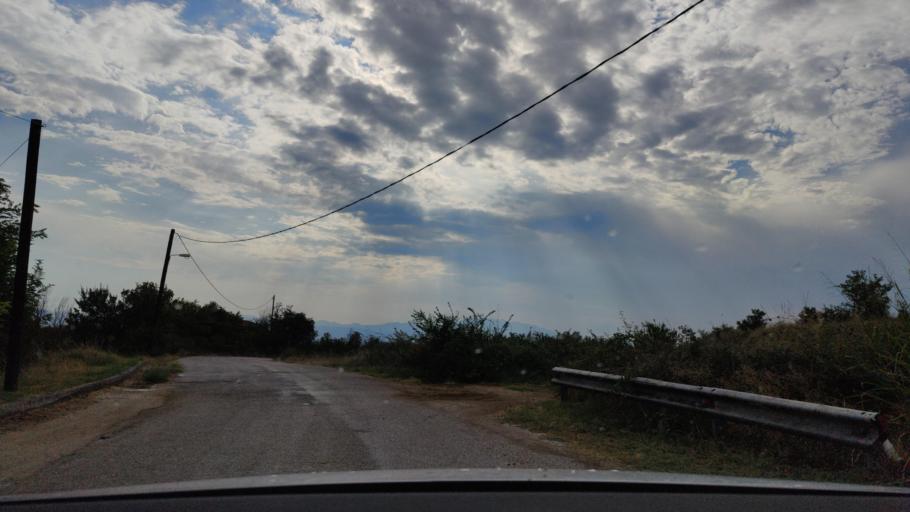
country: GR
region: Central Macedonia
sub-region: Nomos Serron
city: Kala Dendra
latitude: 41.1215
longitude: 23.4592
